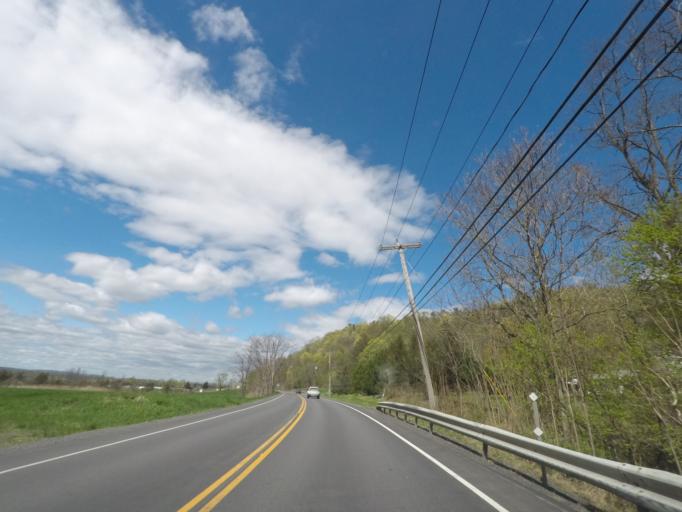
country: US
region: New York
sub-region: Columbia County
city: Oakdale
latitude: 42.2150
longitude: -73.7898
